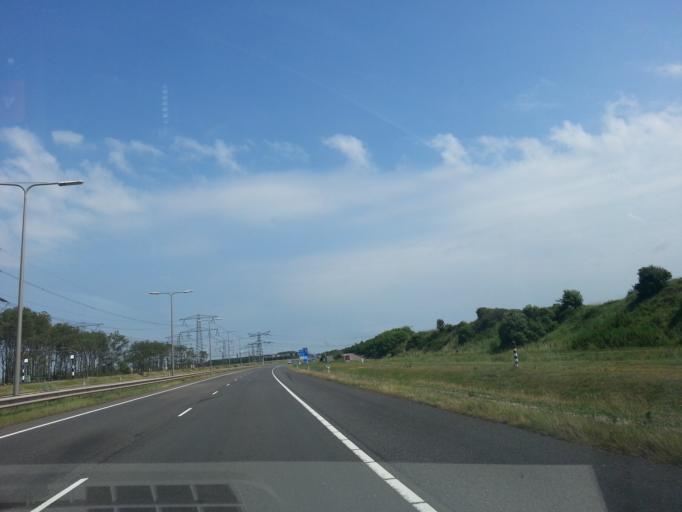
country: NL
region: South Holland
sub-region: Gemeente Rotterdam
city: Hoek van Holland
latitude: 51.9340
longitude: 4.0795
